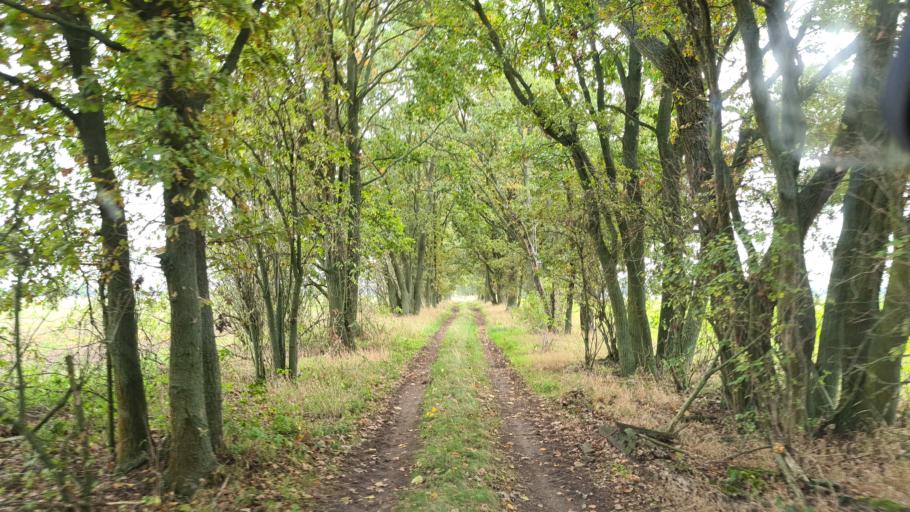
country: DE
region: Brandenburg
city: Schonewalde
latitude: 51.6832
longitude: 13.5626
